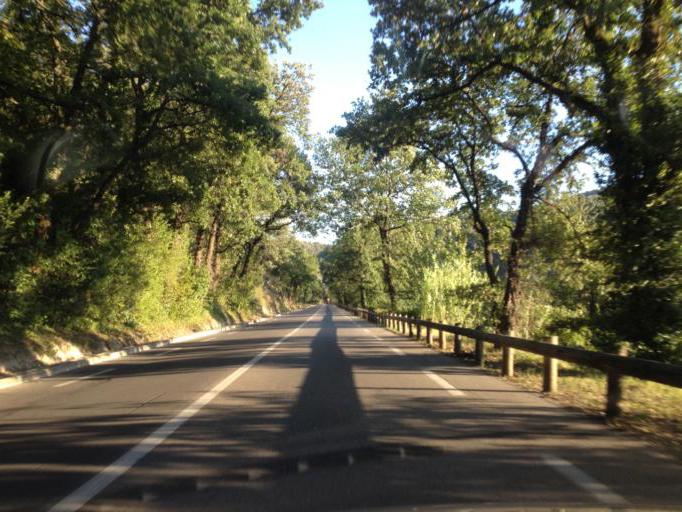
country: FR
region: Provence-Alpes-Cote d'Azur
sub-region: Departement du Vaucluse
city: Vaison-la-Romaine
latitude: 44.2435
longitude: 5.0500
